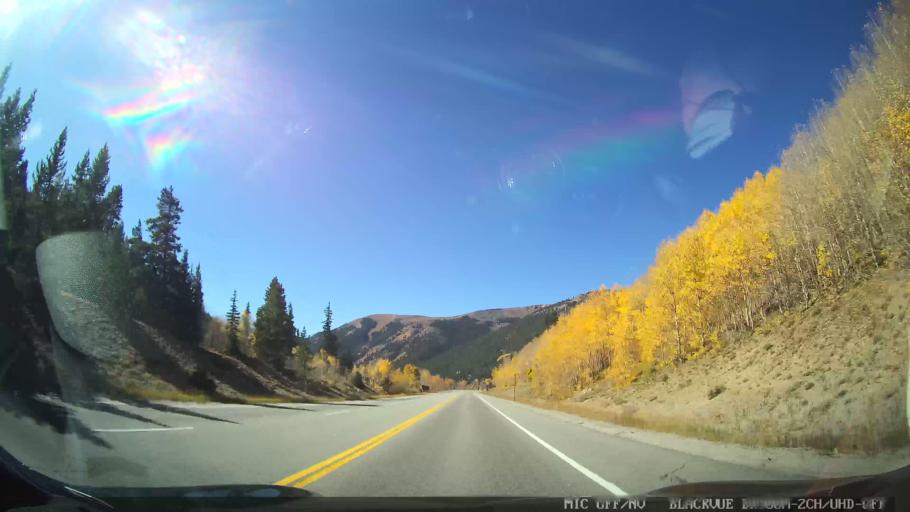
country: US
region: Colorado
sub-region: Lake County
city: Leadville
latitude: 39.3568
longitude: -106.2109
